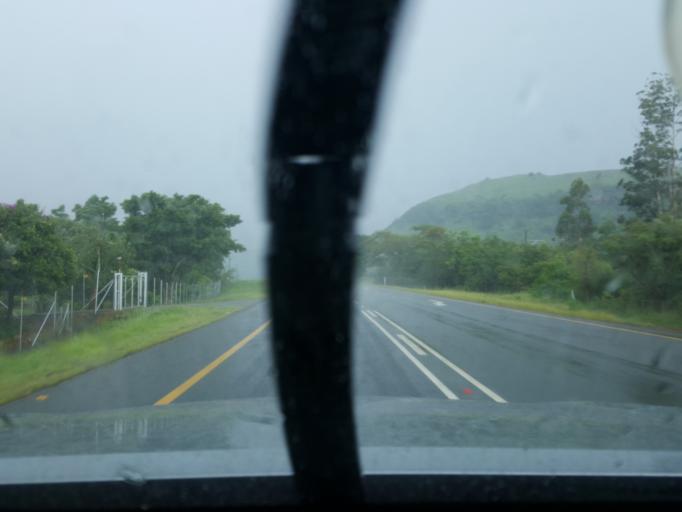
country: ZA
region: Mpumalanga
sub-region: Nkangala District Municipality
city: Belfast
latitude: -25.6065
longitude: 30.4359
